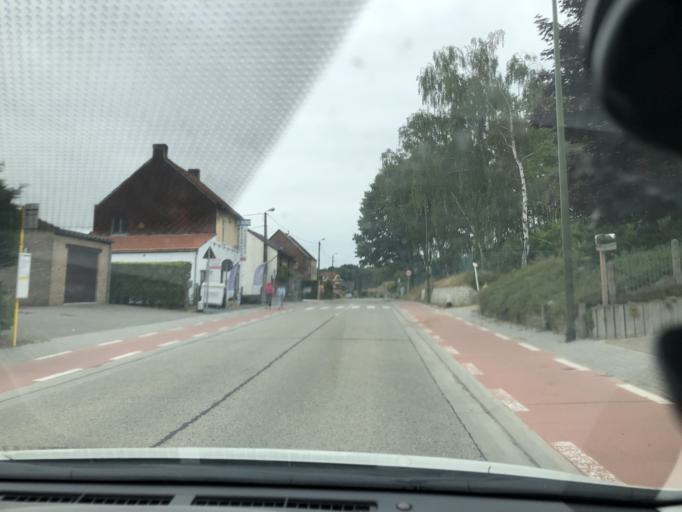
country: BE
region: Flanders
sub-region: Provincie Vlaams-Brabant
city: Oud-Heverlee
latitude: 50.8432
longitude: 4.6698
